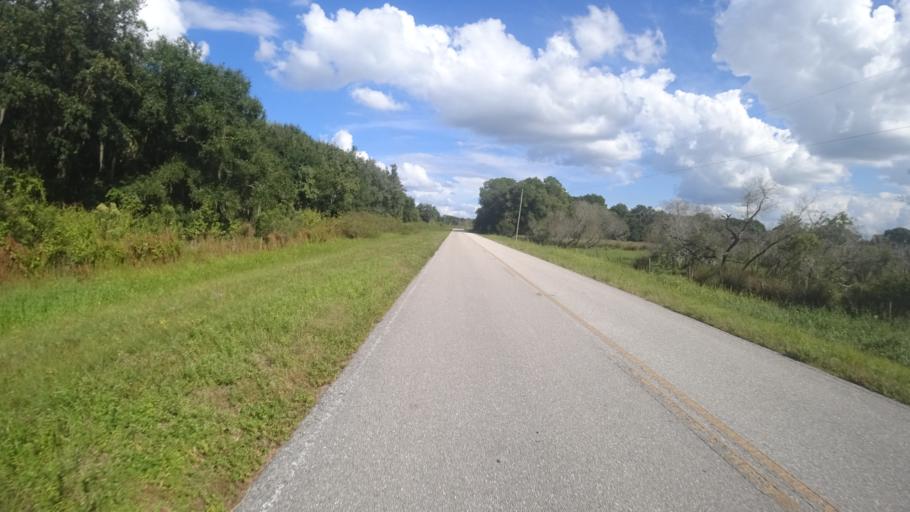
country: US
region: Florida
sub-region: DeSoto County
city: Nocatee
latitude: 27.2736
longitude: -82.1117
